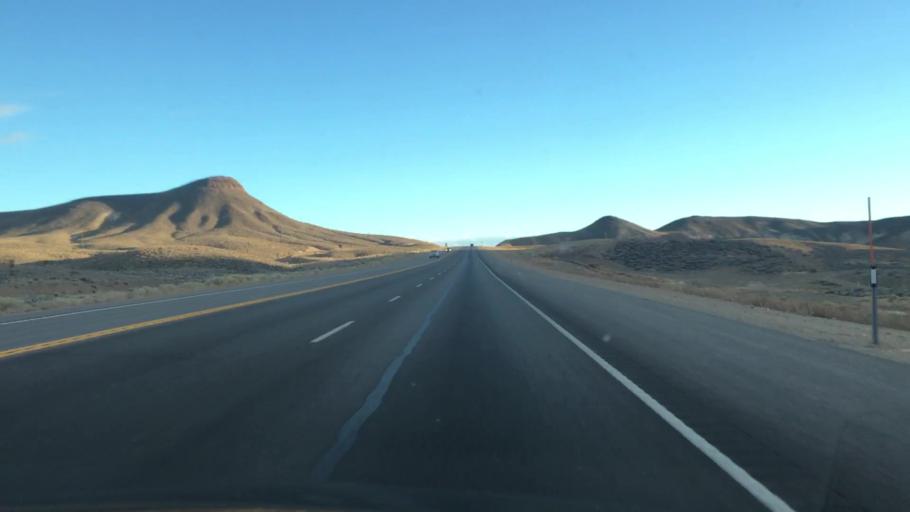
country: US
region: Nevada
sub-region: Esmeralda County
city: Goldfield
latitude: 37.6887
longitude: -117.2336
